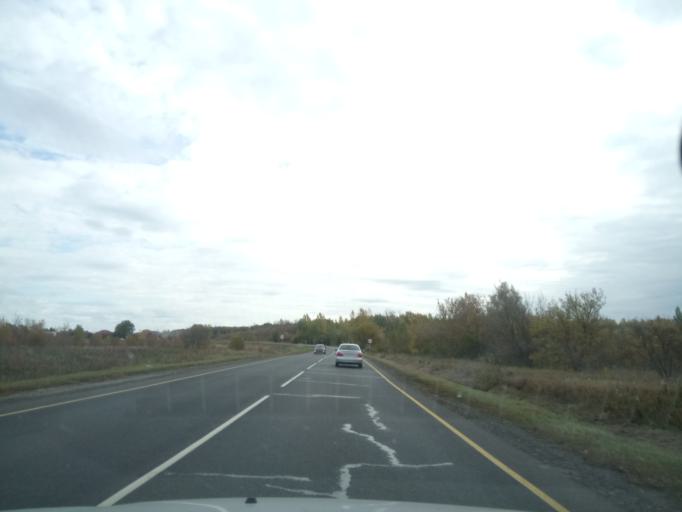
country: RU
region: Nizjnij Novgorod
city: Lukoyanov
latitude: 55.0517
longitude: 44.3748
